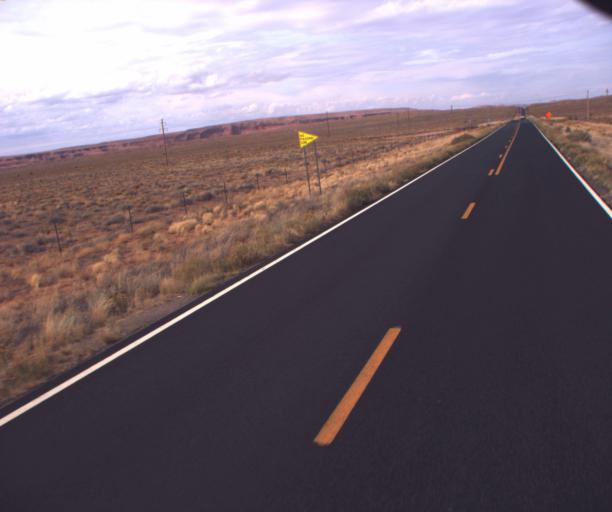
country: US
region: Arizona
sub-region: Apache County
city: Many Farms
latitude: 36.5867
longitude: -109.5592
